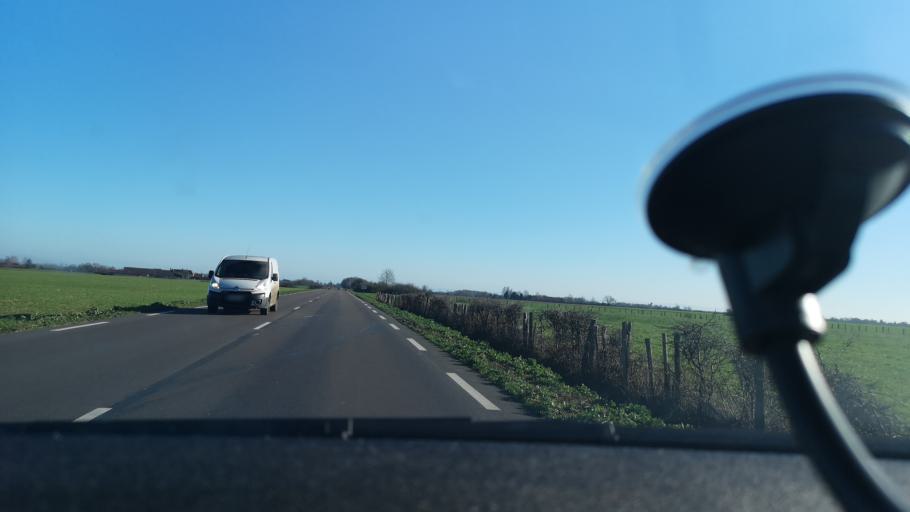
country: FR
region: Bourgogne
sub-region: Departement de Saone-et-Loire
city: Saint-Martin-en-Bresse
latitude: 46.7461
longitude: 5.0570
